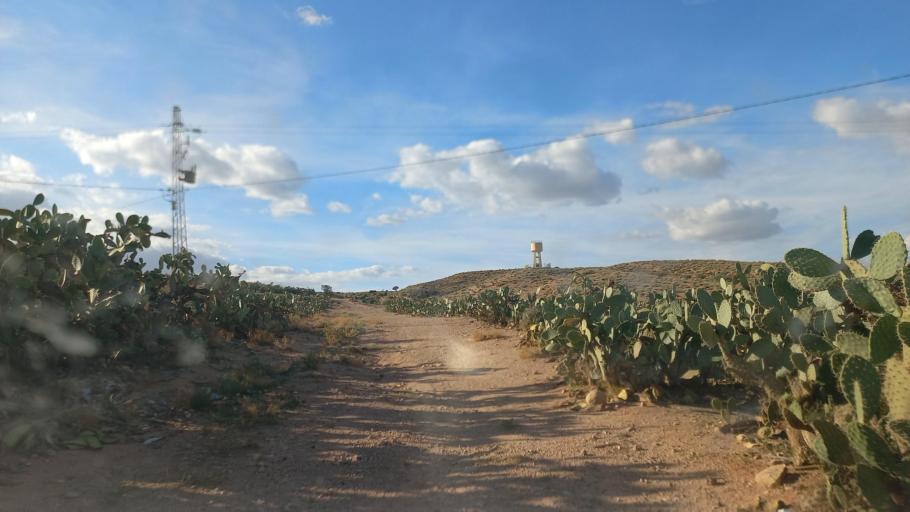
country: TN
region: Al Qasrayn
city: Sbiba
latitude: 35.3814
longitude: 9.0210
